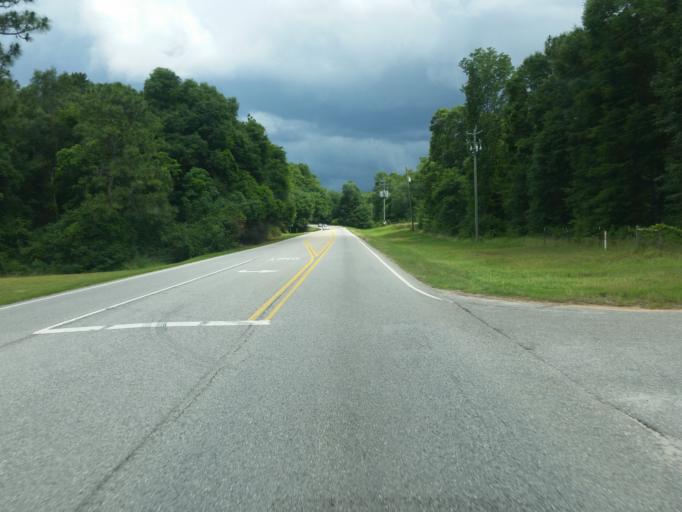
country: US
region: Mississippi
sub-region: Jackson County
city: Hurley
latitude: 30.8299
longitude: -88.3841
